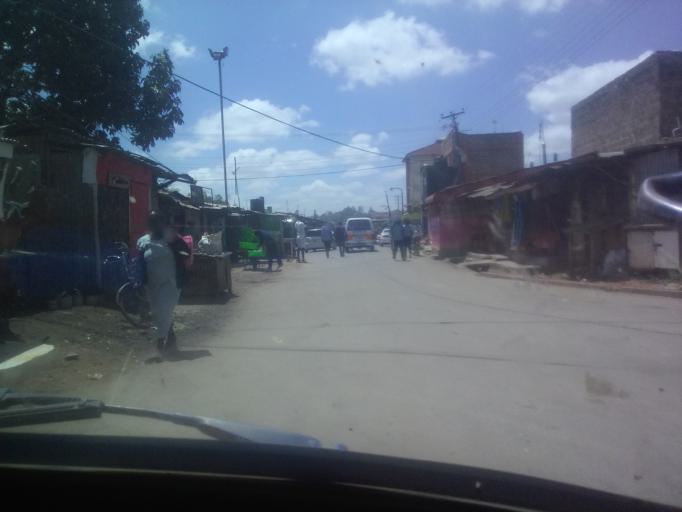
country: KE
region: Nairobi Area
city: Nairobi
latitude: -1.3098
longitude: 36.7758
